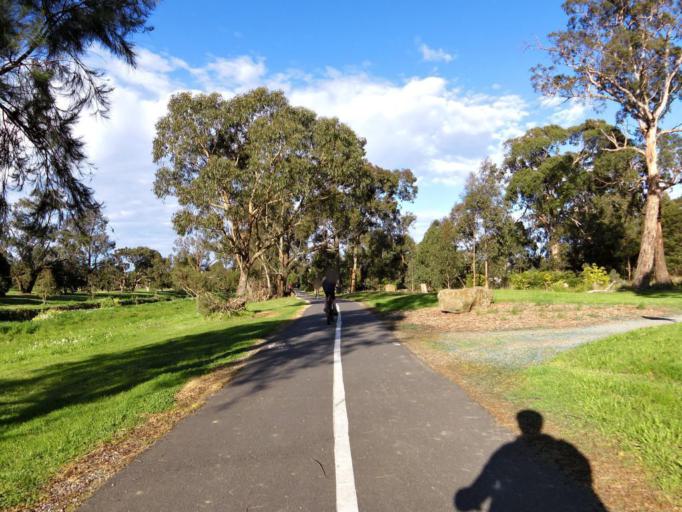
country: AU
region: Victoria
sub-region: Knox
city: Wantirna
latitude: -37.8383
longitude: 145.2189
